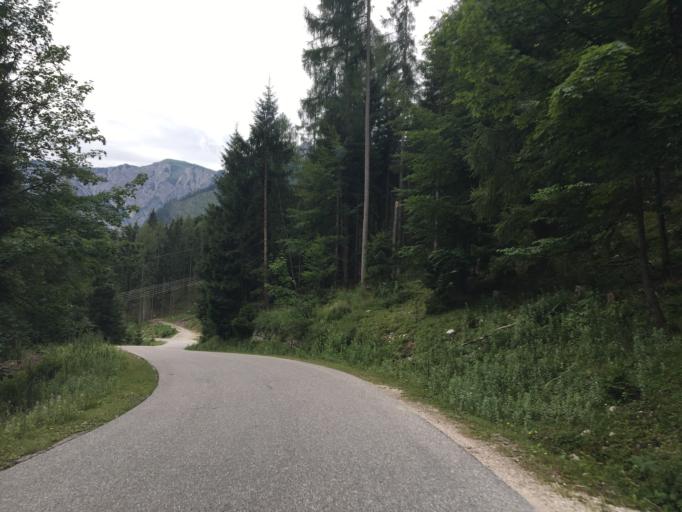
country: AT
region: Salzburg
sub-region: Politischer Bezirk Salzburg-Umgebung
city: Strobl
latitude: 47.6638
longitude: 13.4527
